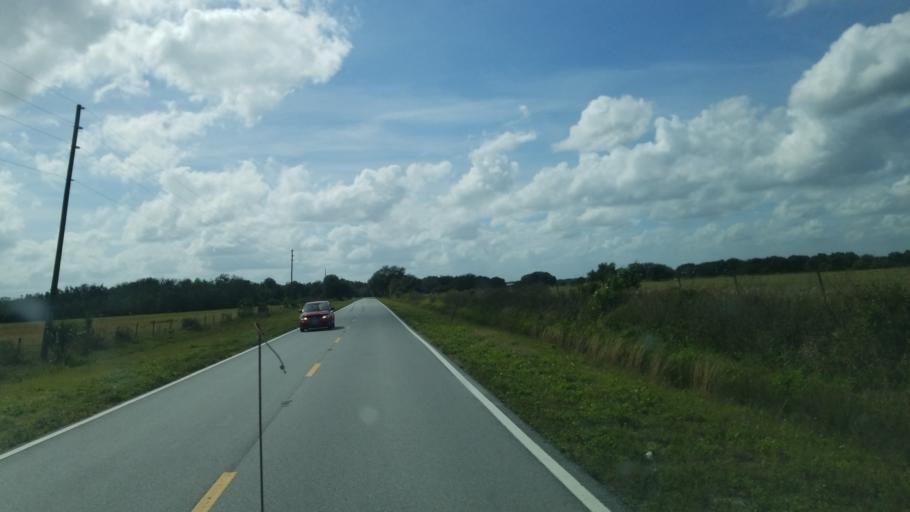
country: US
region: Florida
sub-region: Polk County
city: Babson Park
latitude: 27.9620
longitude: -81.4101
